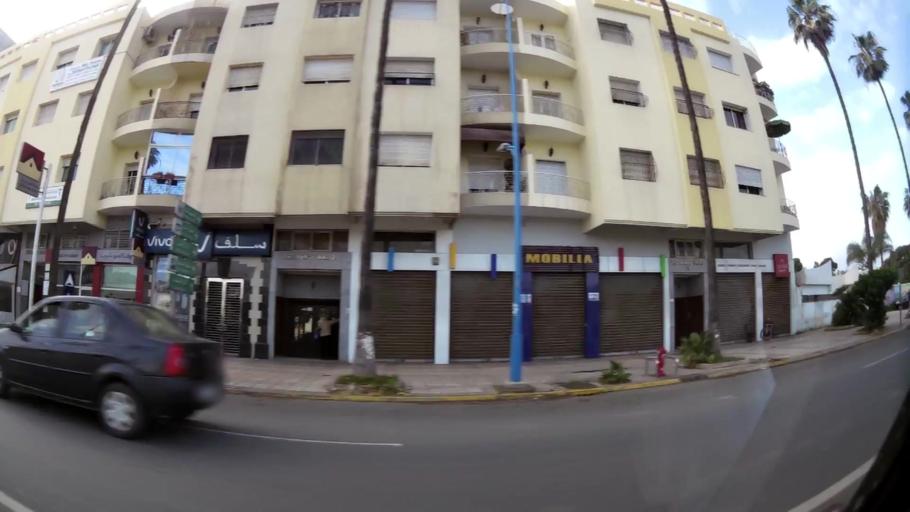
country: MA
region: Grand Casablanca
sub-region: Mohammedia
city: Mohammedia
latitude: 33.6946
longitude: -7.3902
